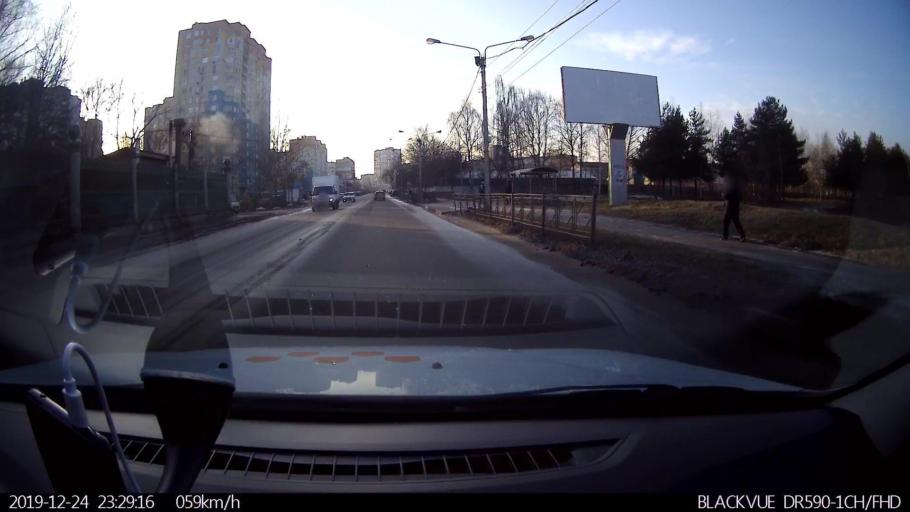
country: RU
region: Nizjnij Novgorod
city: Gorbatovka
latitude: 56.2398
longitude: 43.8442
